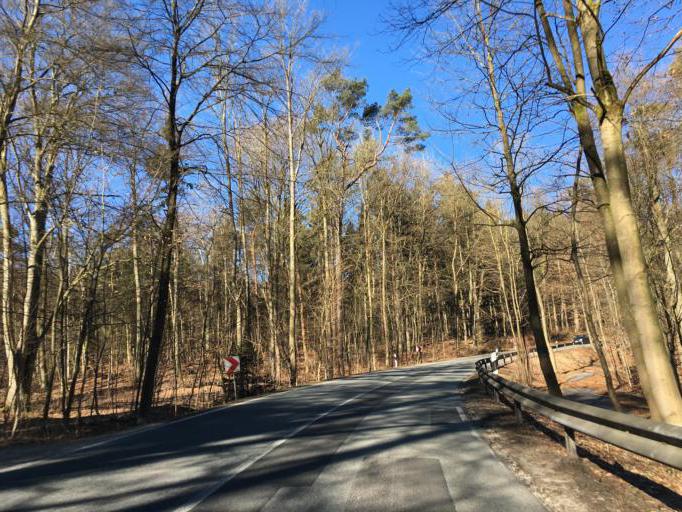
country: DE
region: Schleswig-Holstein
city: Molln
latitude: 53.6026
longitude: 10.7080
